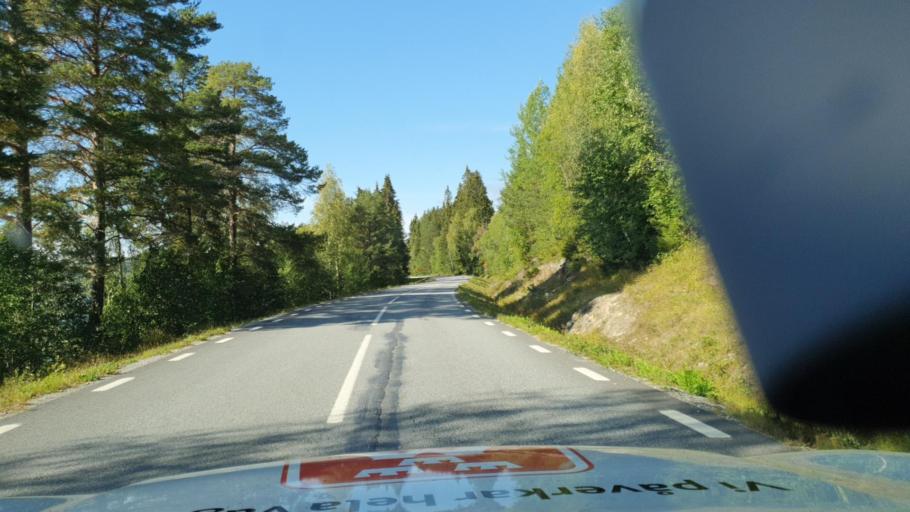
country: SE
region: Vaesterbotten
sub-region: Dorotea Kommun
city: Dorotea
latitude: 64.1125
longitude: 16.2304
